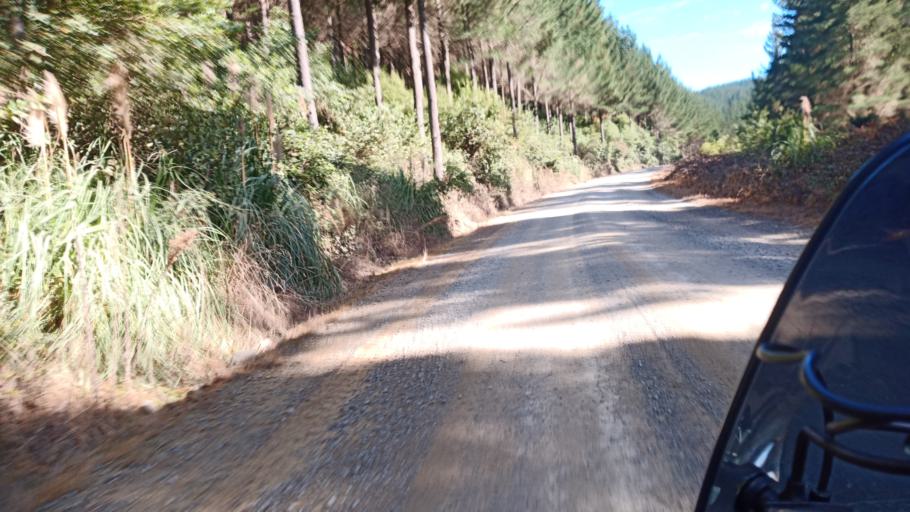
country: NZ
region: Hawke's Bay
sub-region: Wairoa District
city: Wairoa
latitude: -38.9235
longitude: 177.2062
